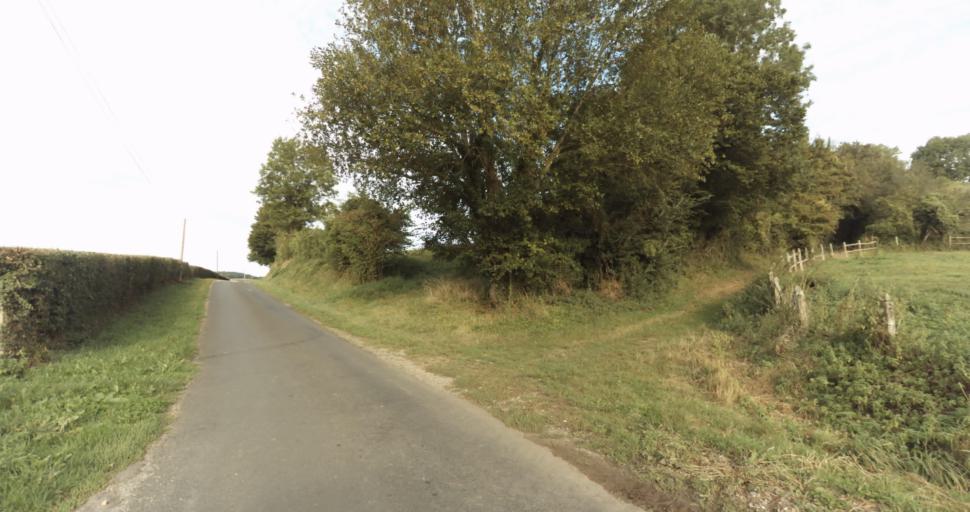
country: FR
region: Lower Normandy
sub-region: Departement de l'Orne
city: Vimoutiers
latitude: 48.8759
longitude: 0.2333
